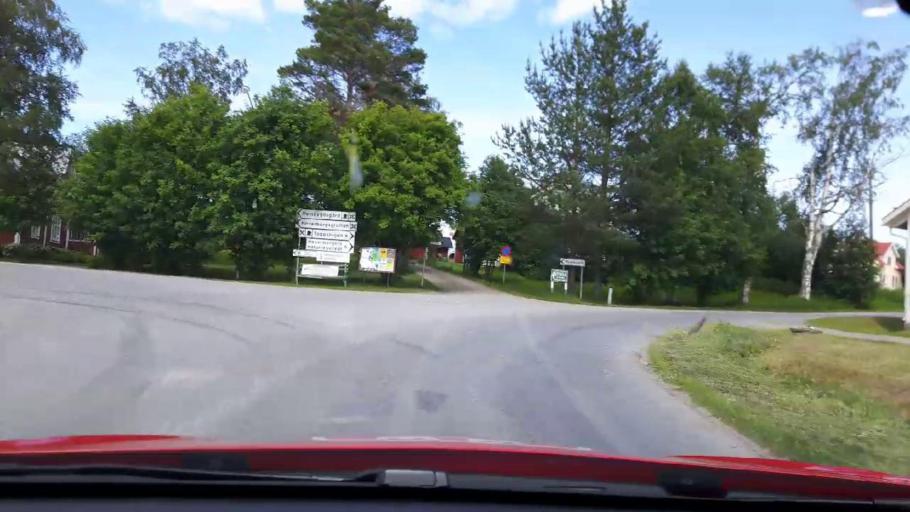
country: SE
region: Jaemtland
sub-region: Bergs Kommun
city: Hoverberg
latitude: 62.8137
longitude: 14.4472
